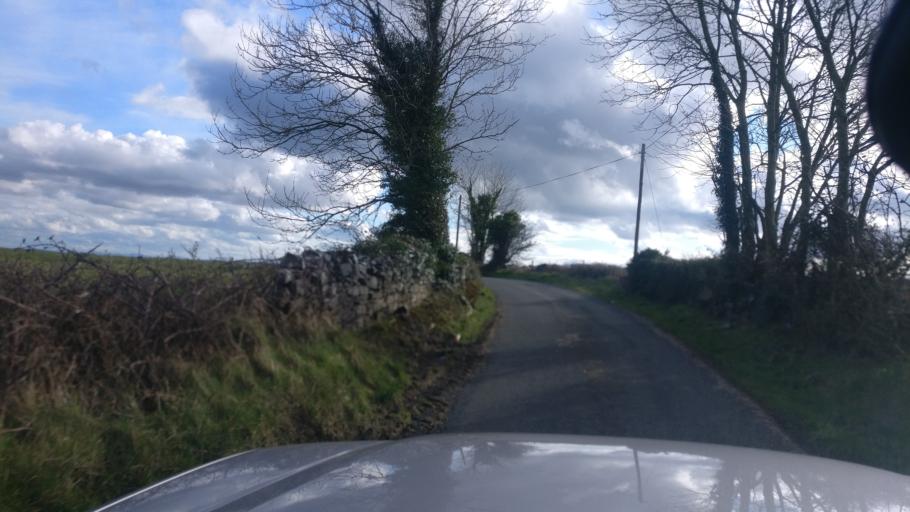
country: IE
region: Connaught
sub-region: County Galway
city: Loughrea
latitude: 53.1739
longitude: -8.4271
